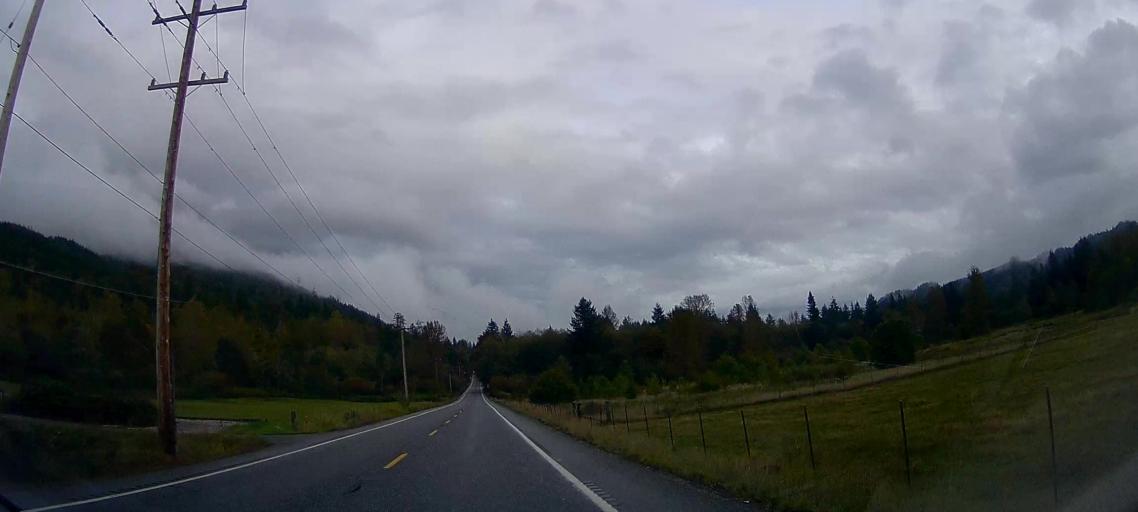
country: US
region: Washington
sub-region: Snohomish County
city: Darrington
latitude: 48.5181
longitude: -121.7011
